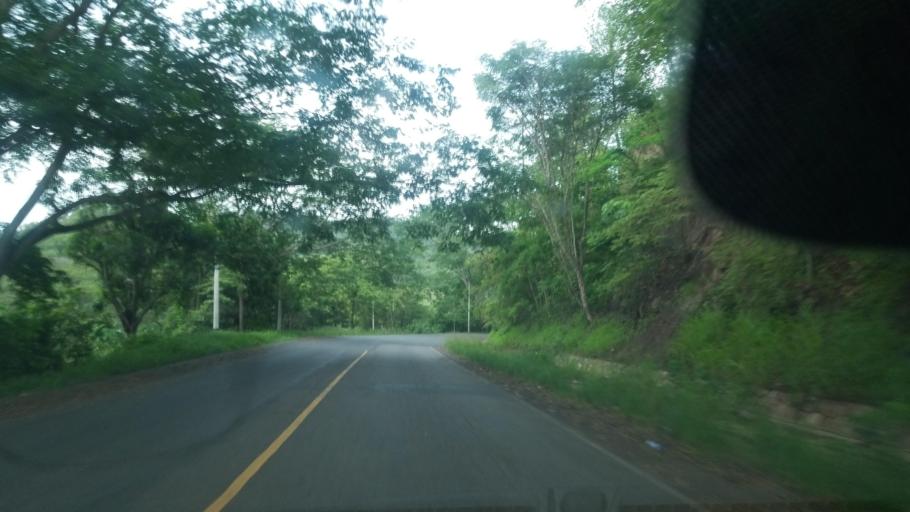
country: HN
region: Santa Barbara
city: Concepcion del Sur
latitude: 14.8161
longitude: -88.1785
